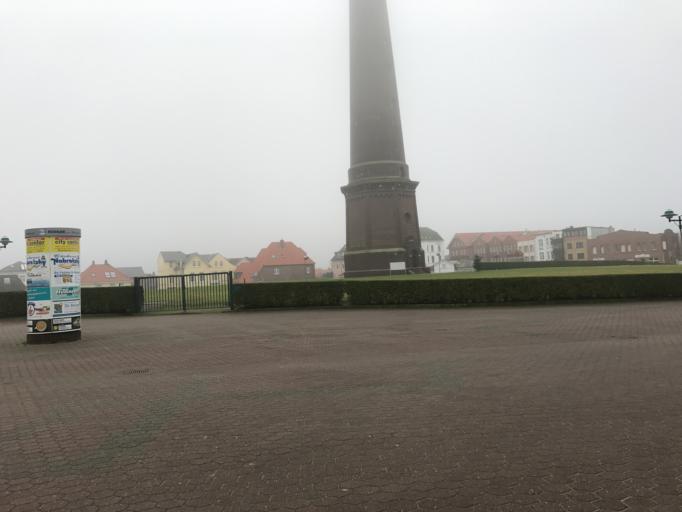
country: DE
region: Lower Saxony
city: Borkum
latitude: 53.5894
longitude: 6.6613
